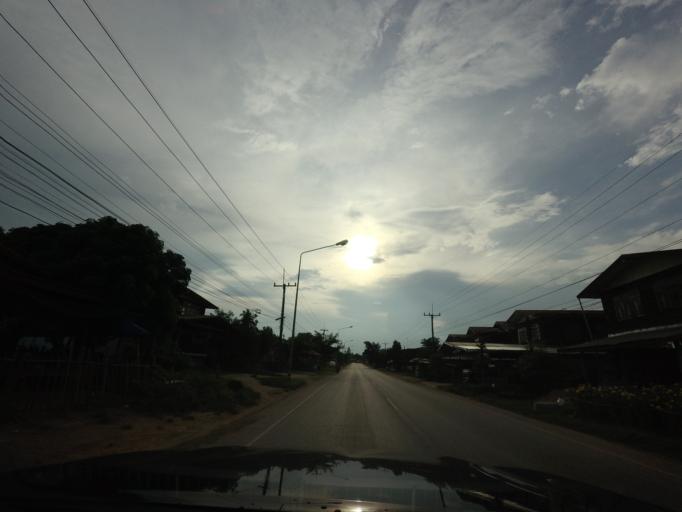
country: TH
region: Nong Khai
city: Pho Tak
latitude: 17.7803
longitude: 102.3846
